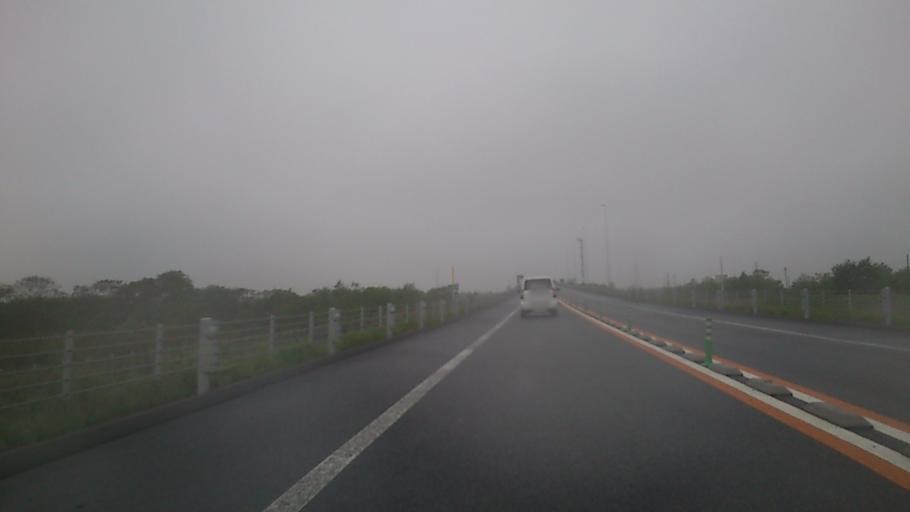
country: JP
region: Hokkaido
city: Kushiro
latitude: 43.0329
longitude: 144.3920
